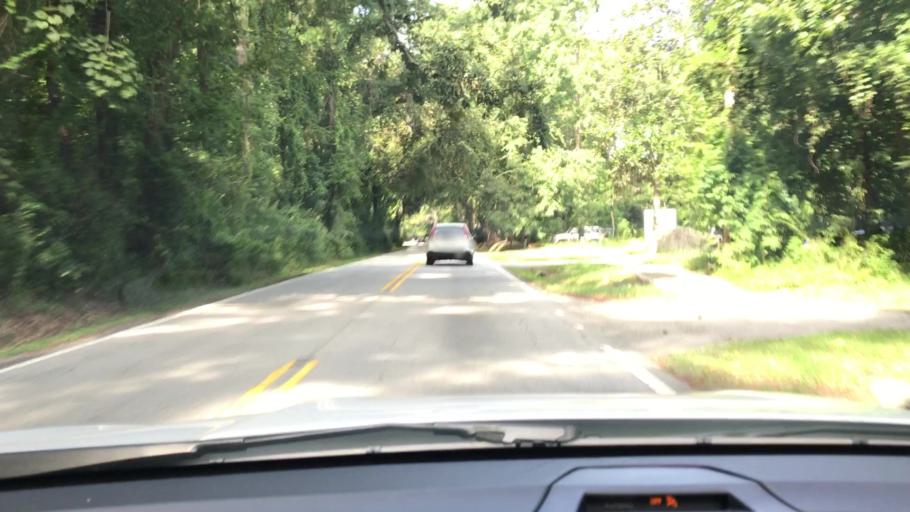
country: US
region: South Carolina
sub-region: Charleston County
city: Mount Pleasant
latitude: 32.8438
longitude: -79.8376
